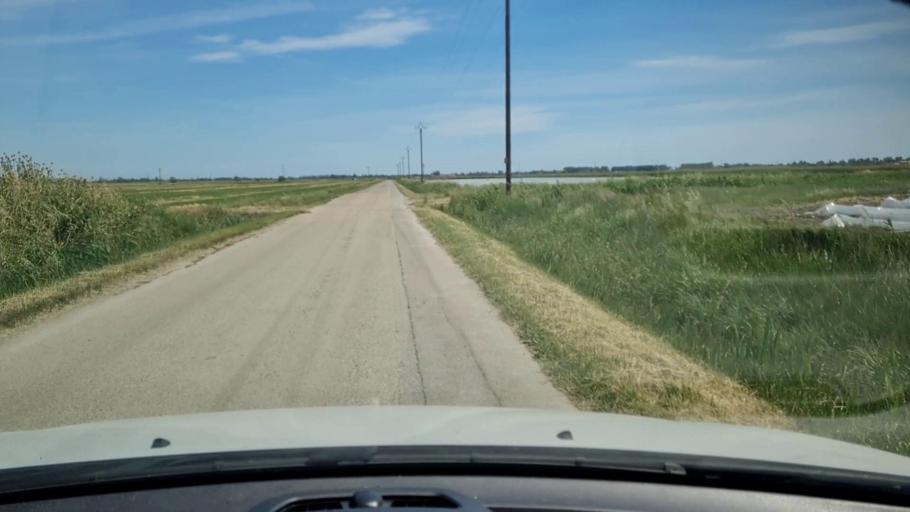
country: FR
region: Languedoc-Roussillon
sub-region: Departement du Gard
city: Saint-Gilles
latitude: 43.6062
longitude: 4.4332
